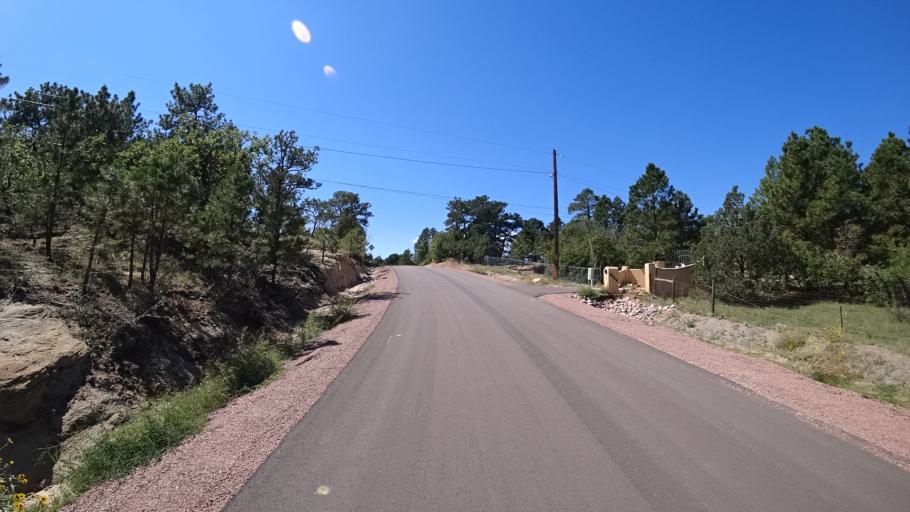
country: US
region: Colorado
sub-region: El Paso County
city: Cimarron Hills
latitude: 38.8615
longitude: -104.7392
